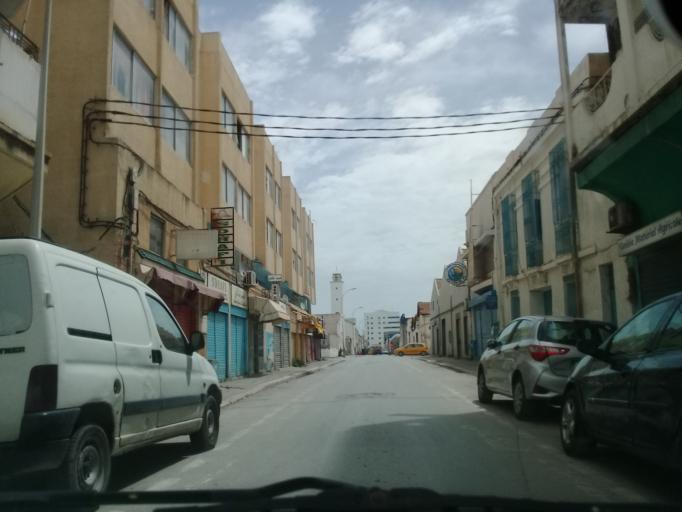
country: TN
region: Tunis
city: Tunis
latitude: 36.7952
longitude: 10.1841
